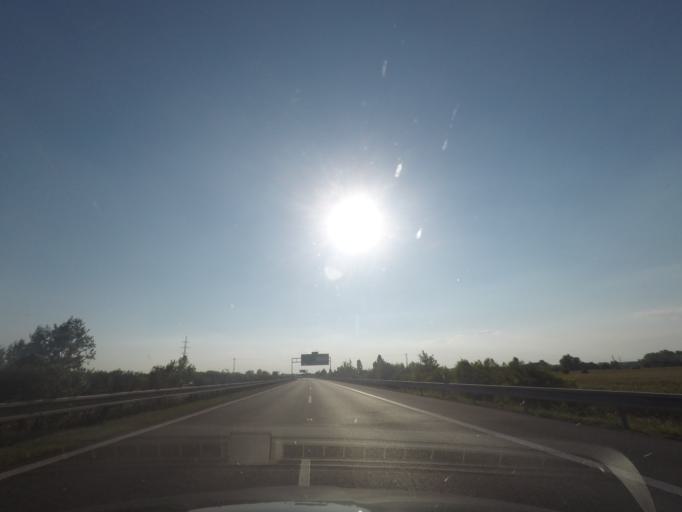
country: CZ
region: Olomoucky
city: Grygov
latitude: 49.5549
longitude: 17.2783
